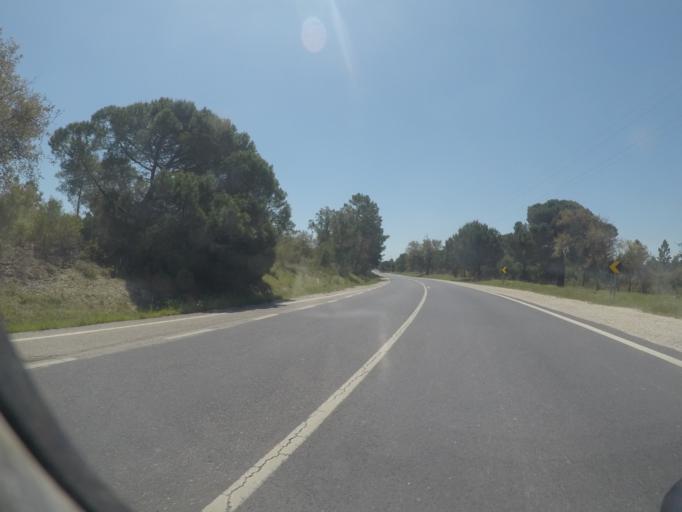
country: PT
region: Setubal
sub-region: Sesimbra
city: Sesimbra
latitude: 38.5101
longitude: -9.1053
